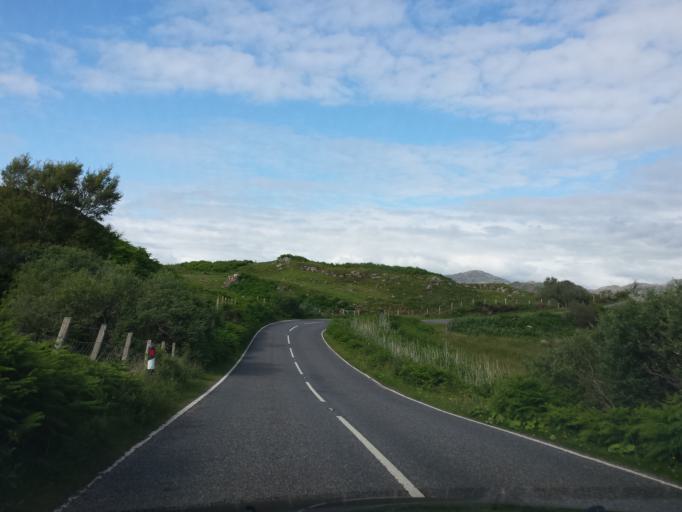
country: GB
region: Scotland
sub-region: Argyll and Bute
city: Isle Of Mull
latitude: 56.9622
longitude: -5.8344
